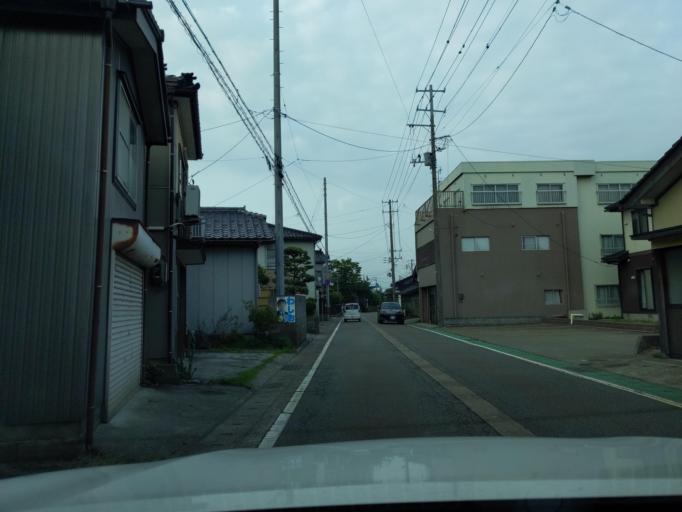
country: JP
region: Niigata
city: Kashiwazaki
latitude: 37.3805
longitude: 138.5713
